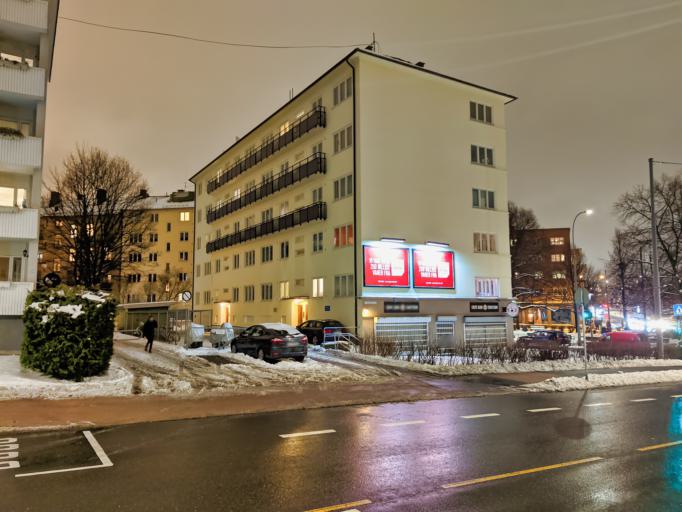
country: NO
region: Oslo
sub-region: Oslo
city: Oslo
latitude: 59.9419
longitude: 10.7702
